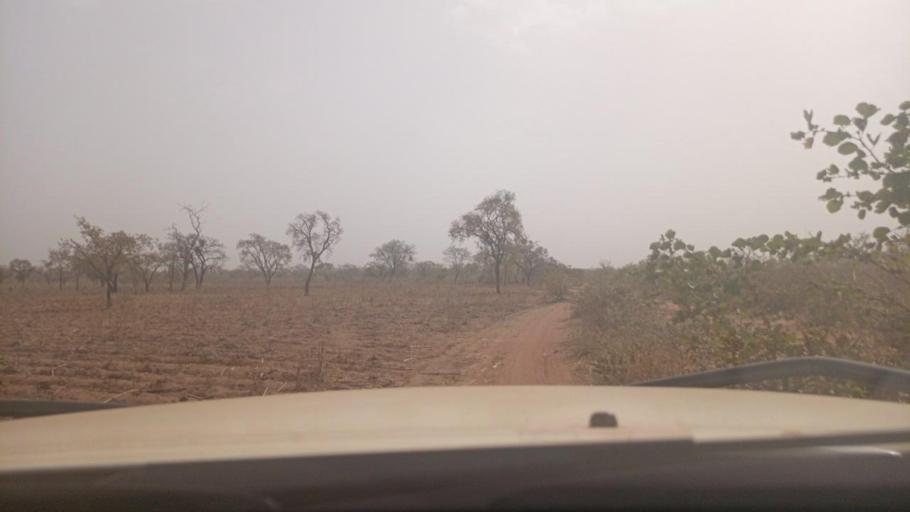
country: BF
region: Boucle du Mouhoun
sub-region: Province des Banwa
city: Salanso
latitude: 12.1630
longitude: -4.2392
